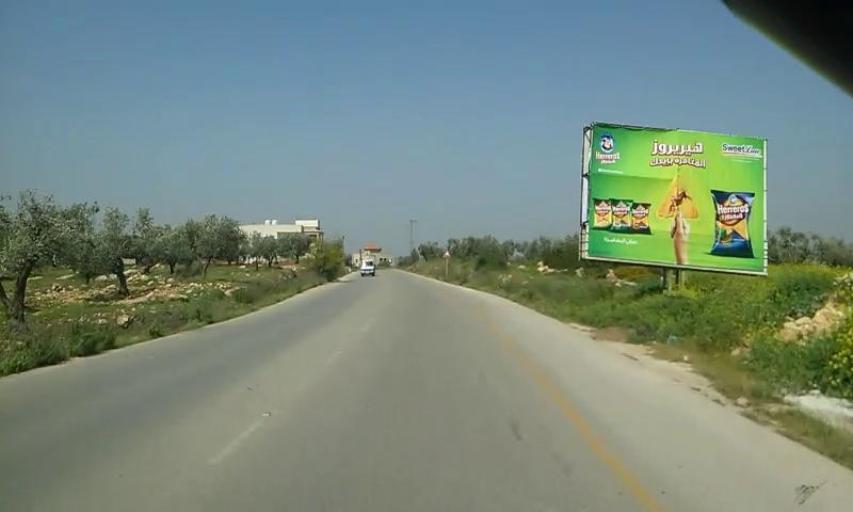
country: PS
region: West Bank
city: Az Zababidah
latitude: 32.3798
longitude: 35.3310
